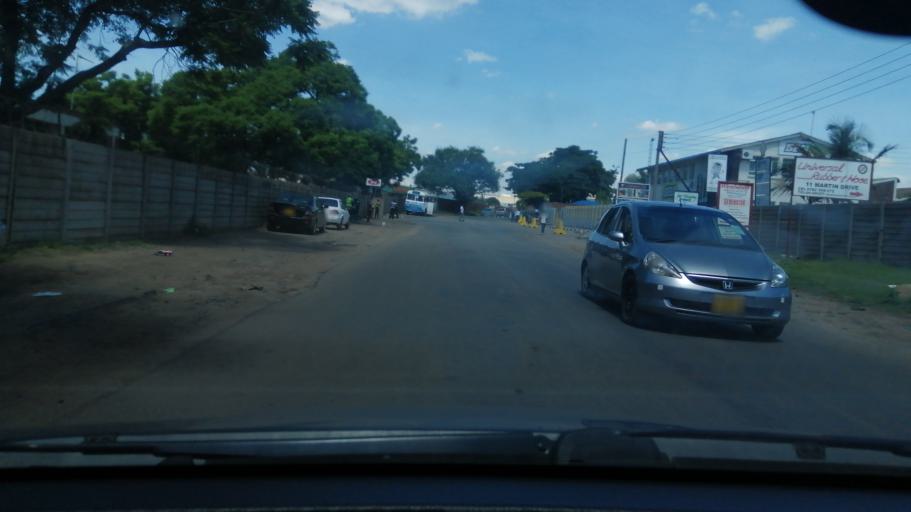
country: ZW
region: Harare
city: Epworth
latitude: -17.8441
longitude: 31.1148
